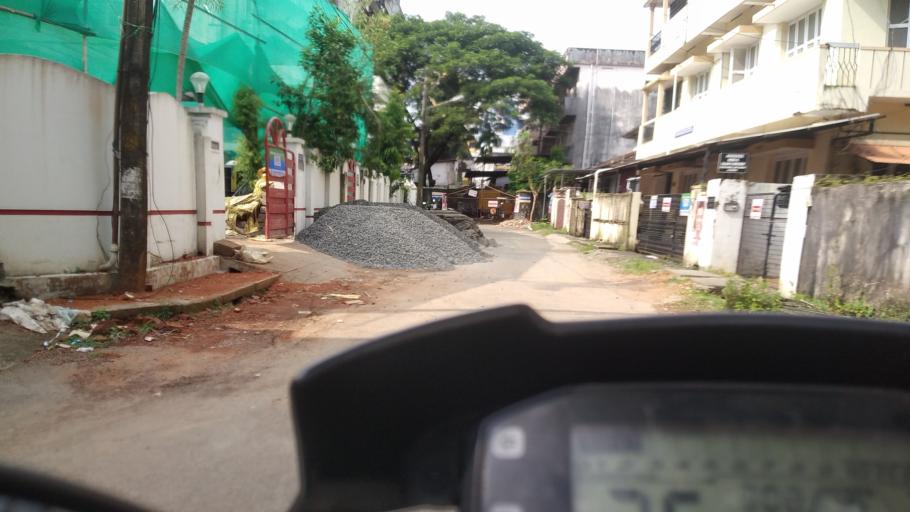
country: IN
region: Kerala
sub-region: Ernakulam
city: Cochin
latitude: 9.9635
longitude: 76.2909
